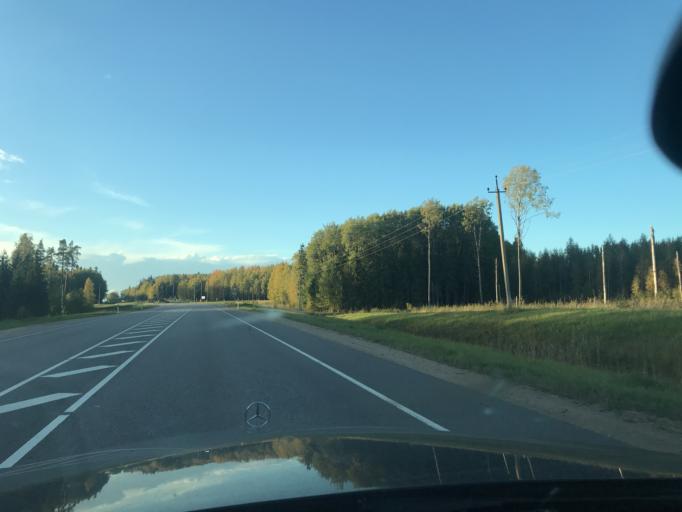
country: EE
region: Vorumaa
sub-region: Voru linn
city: Voru
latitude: 57.8472
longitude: 27.0420
